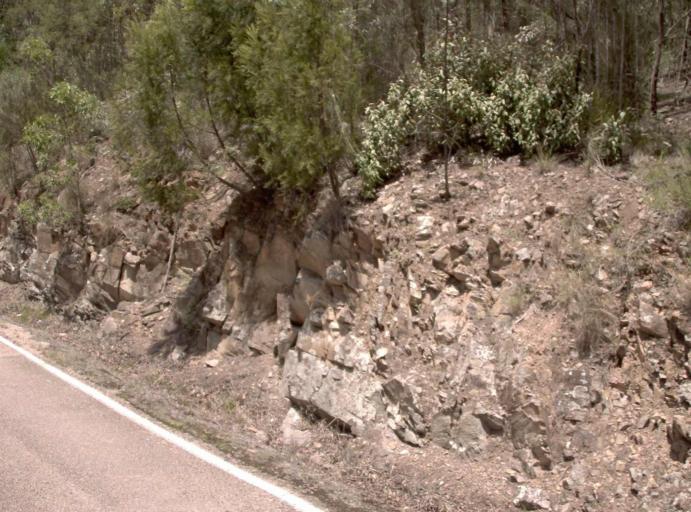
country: AU
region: Victoria
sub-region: East Gippsland
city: Lakes Entrance
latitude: -37.5351
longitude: 147.8559
